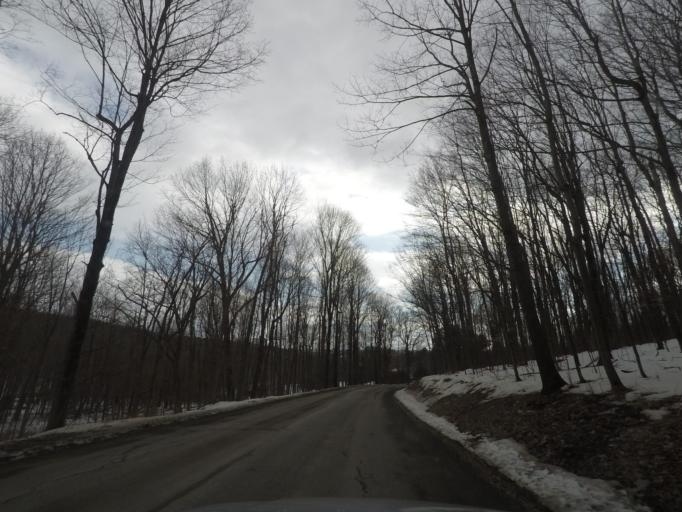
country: US
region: New York
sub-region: Saratoga County
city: Waterford
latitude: 42.7779
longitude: -73.6247
